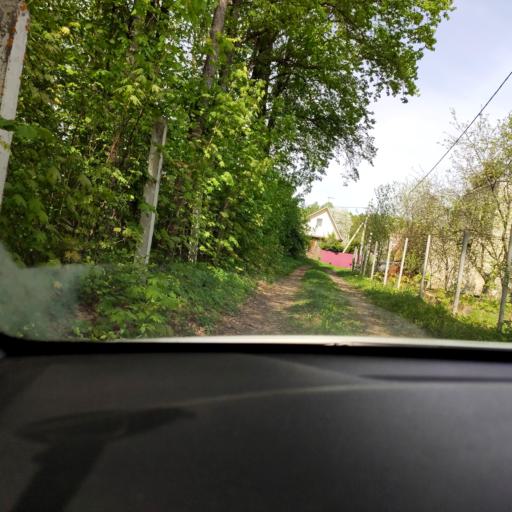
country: RU
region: Tatarstan
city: Osinovo
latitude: 55.7477
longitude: 48.8136
